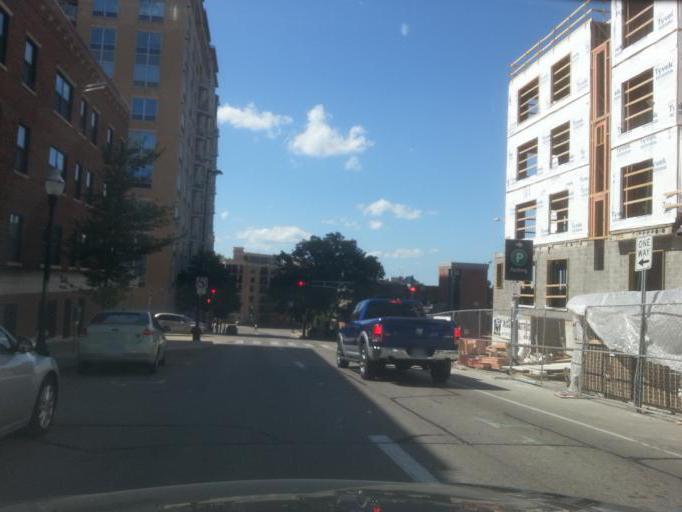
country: US
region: Wisconsin
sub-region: Dane County
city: Madison
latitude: 43.0767
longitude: -89.3826
